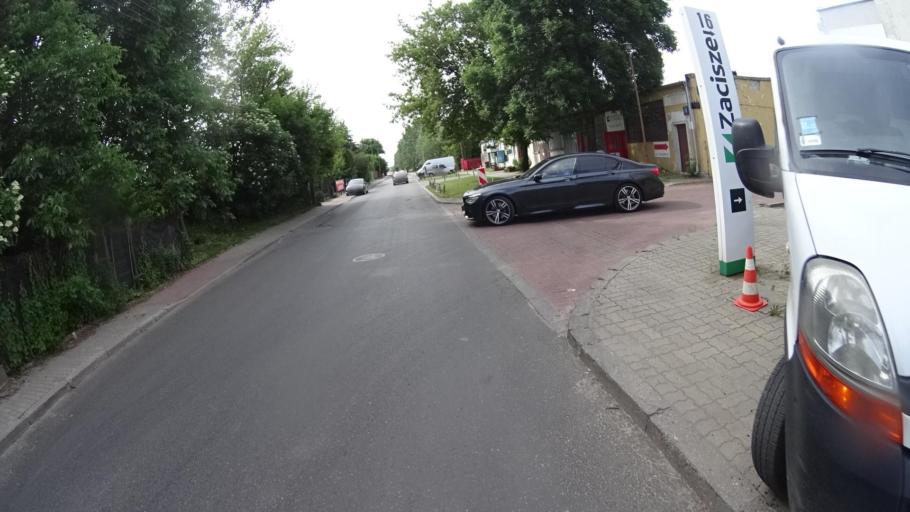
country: PL
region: Masovian Voivodeship
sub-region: Warszawa
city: Wlochy
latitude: 52.1862
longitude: 20.9500
